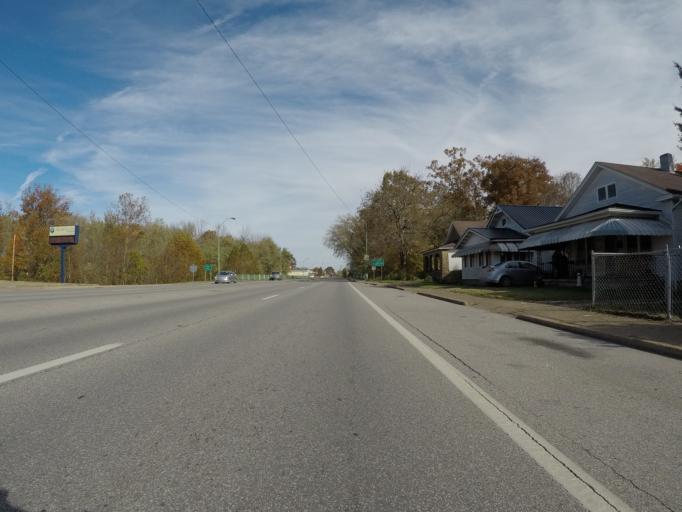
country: US
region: Ohio
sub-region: Lawrence County
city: Burlington
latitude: 38.4060
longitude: -82.5012
